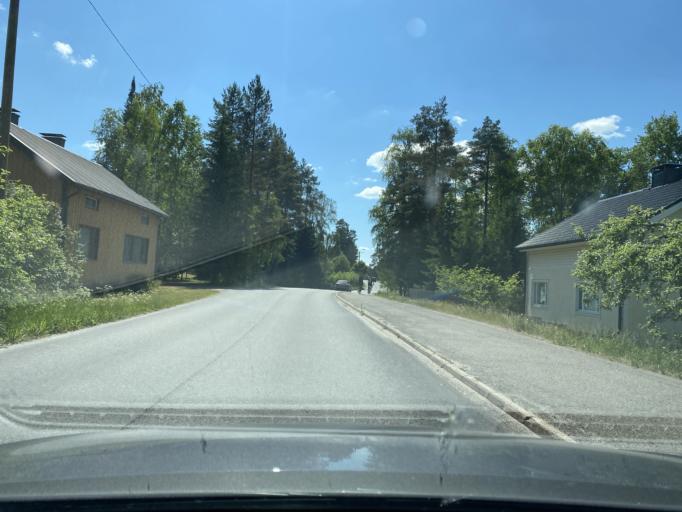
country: FI
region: Satakunta
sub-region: Rauma
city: Eura
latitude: 61.1280
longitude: 22.1635
